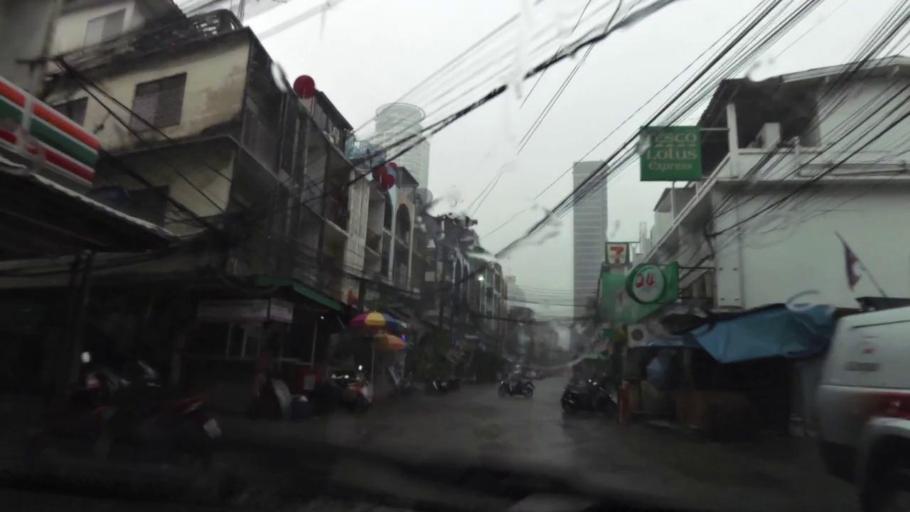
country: TH
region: Bangkok
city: Phra Khanong
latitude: 13.7143
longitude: 100.5965
